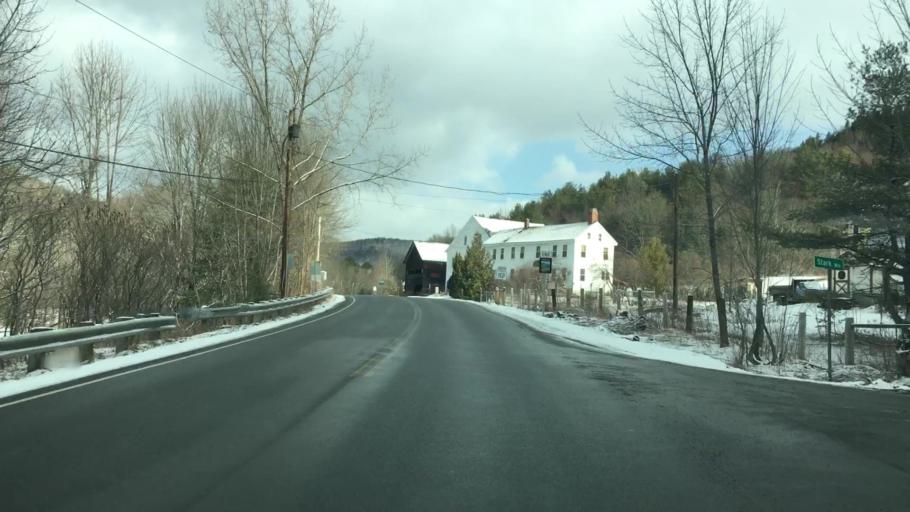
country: US
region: Massachusetts
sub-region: Franklin County
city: Colrain
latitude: 42.7335
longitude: -72.7206
